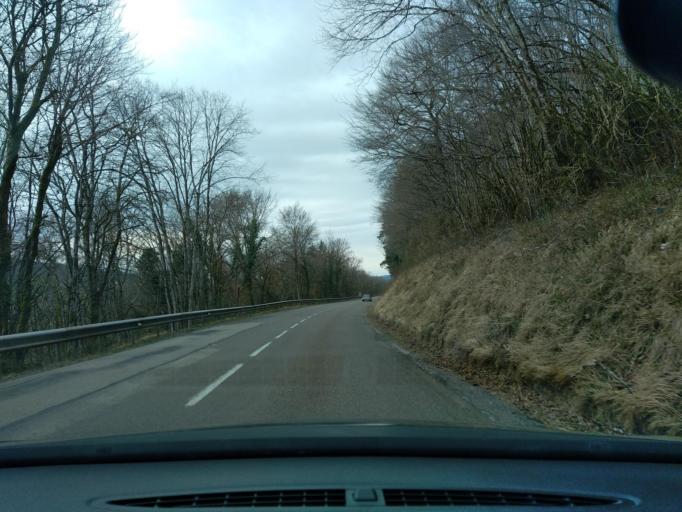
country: FR
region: Franche-Comte
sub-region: Departement du Jura
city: Orgelet
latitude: 46.4797
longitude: 5.5823
